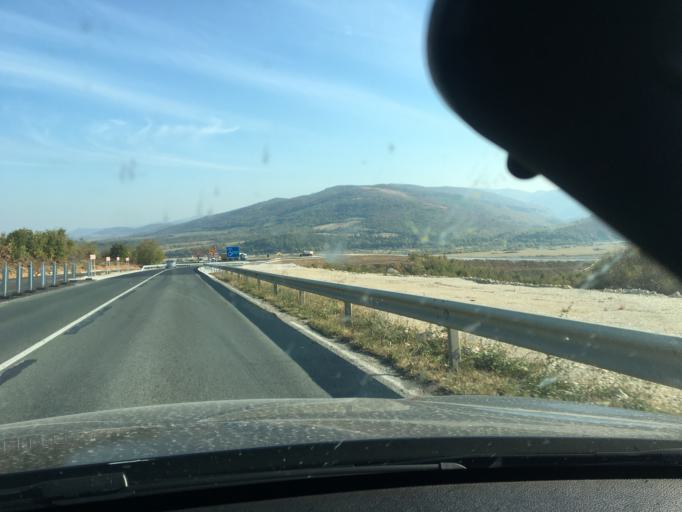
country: BG
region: Lovech
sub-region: Obshtina Yablanitsa
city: Yablanitsa
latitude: 43.0587
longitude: 24.2194
